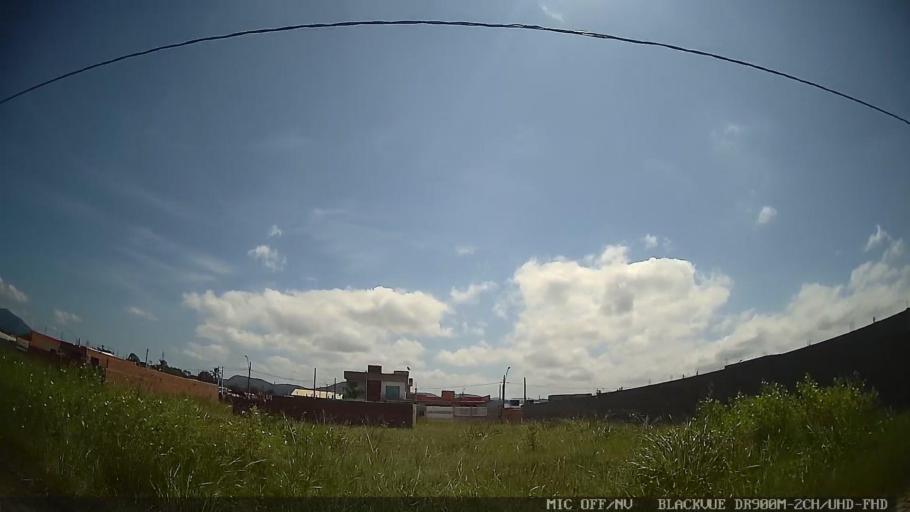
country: BR
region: Sao Paulo
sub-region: Peruibe
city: Peruibe
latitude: -24.3013
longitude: -46.9987
